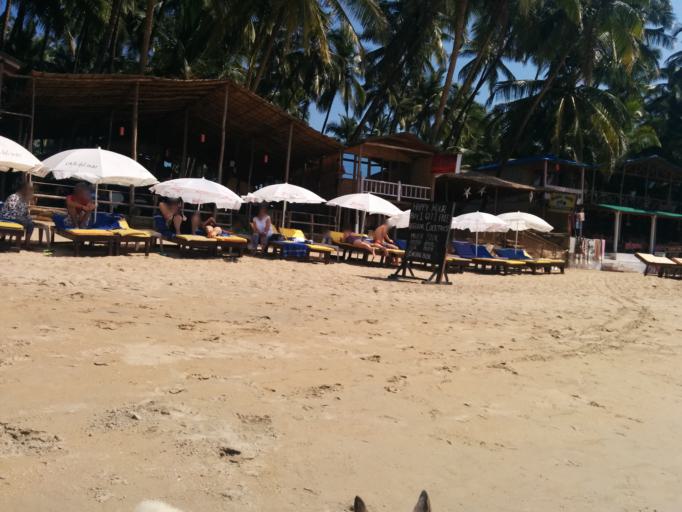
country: IN
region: Karnataka
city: Canacona
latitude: 15.0062
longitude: 74.0268
